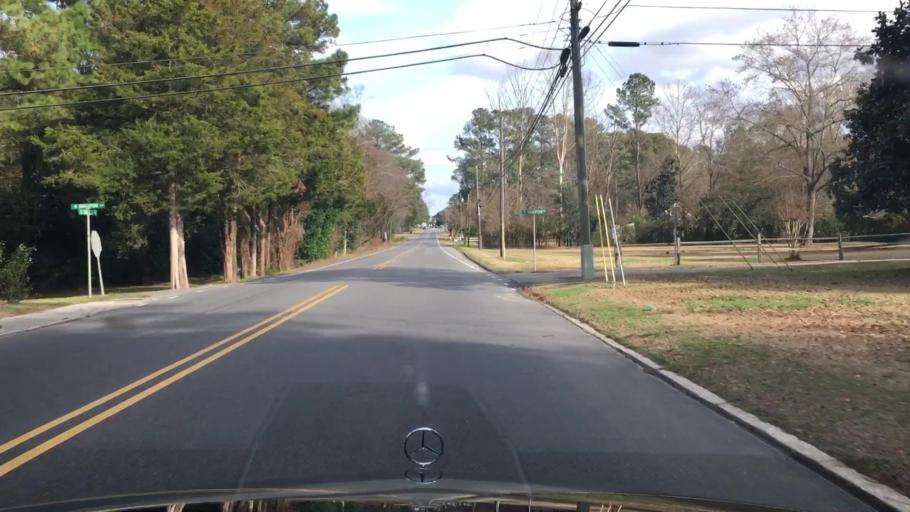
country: US
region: North Carolina
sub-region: Duplin County
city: Warsaw
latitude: 35.0008
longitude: -78.0859
